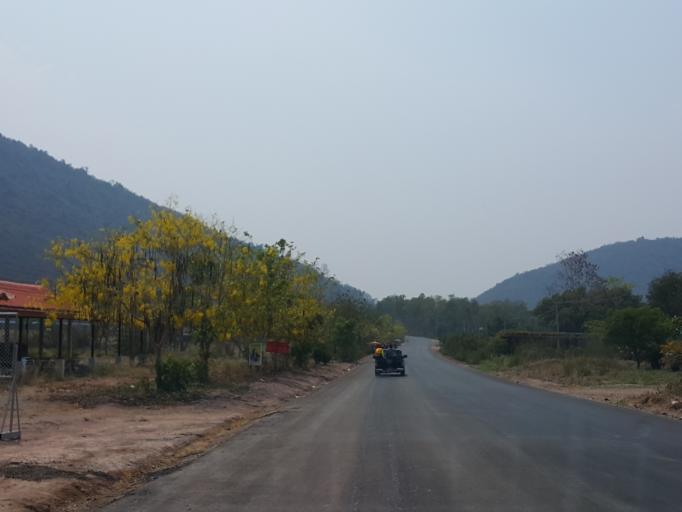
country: TH
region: Nakhon Sawan
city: Mae Wong
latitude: 15.8998
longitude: 99.4652
